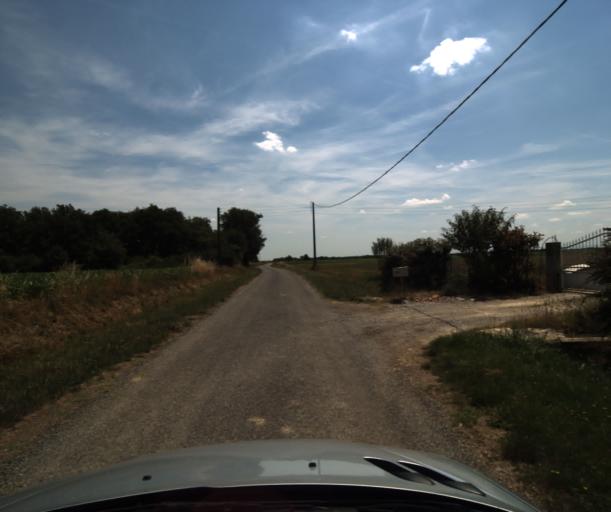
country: FR
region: Midi-Pyrenees
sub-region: Departement de la Haute-Garonne
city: Saint-Lys
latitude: 43.4736
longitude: 1.1913
